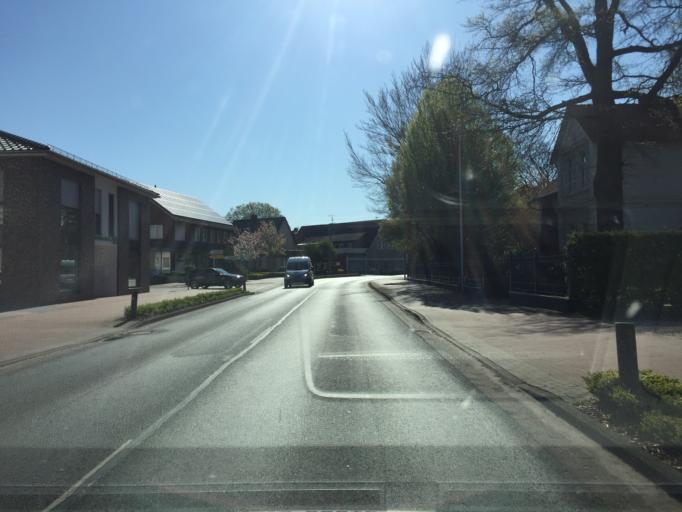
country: DE
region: Lower Saxony
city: Wagenfeld
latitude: 52.5499
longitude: 8.5870
